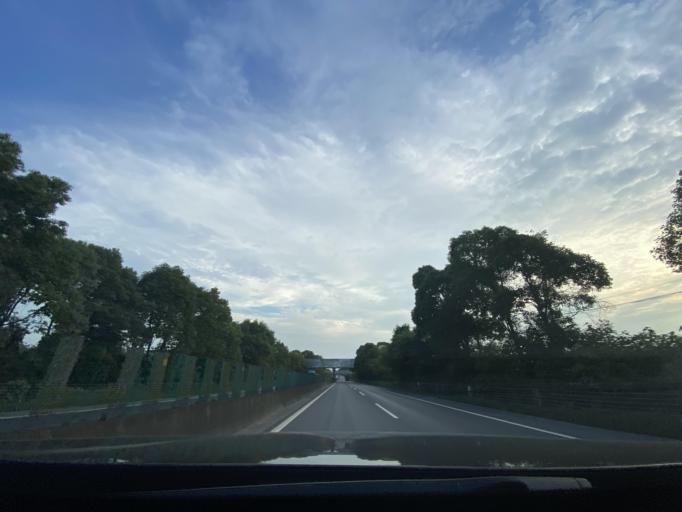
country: CN
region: Sichuan
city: Luojiang
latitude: 31.3673
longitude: 104.5392
